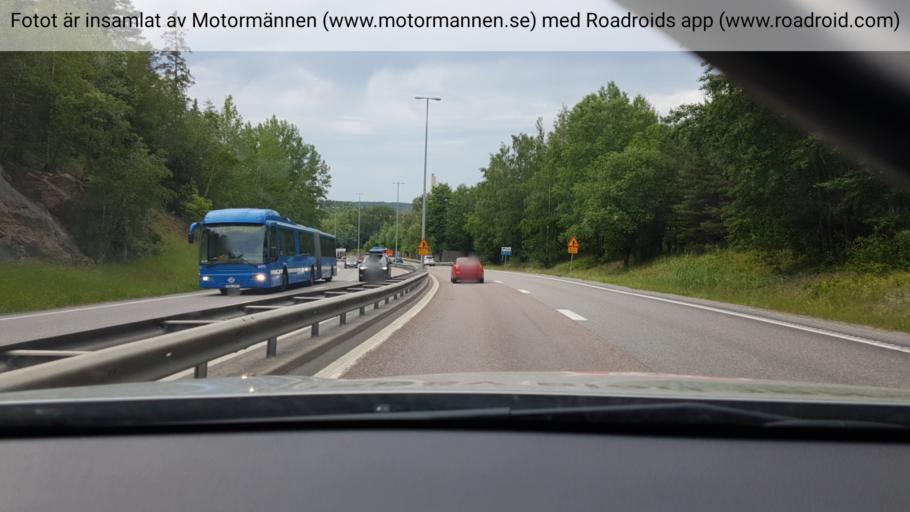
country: SE
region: Stockholm
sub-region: Botkyrka Kommun
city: Fittja
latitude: 59.2488
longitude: 17.8821
